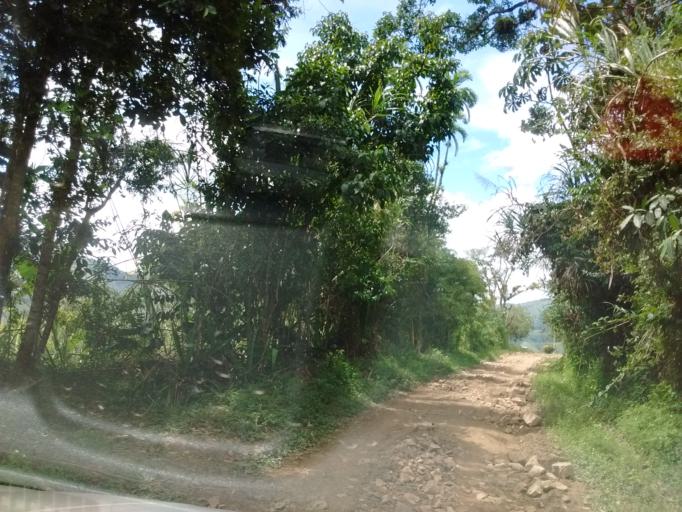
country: CO
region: Cauca
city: Morales
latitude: 2.6723
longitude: -76.7639
